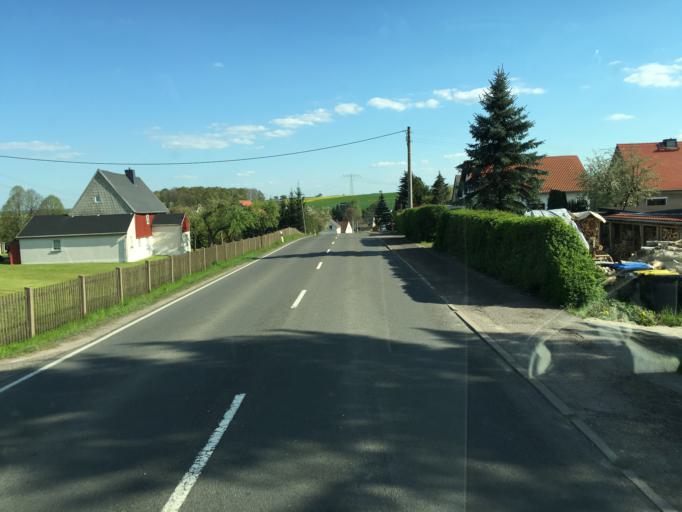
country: DE
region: Saxony
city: Hainichen
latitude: 51.0121
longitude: 13.1288
